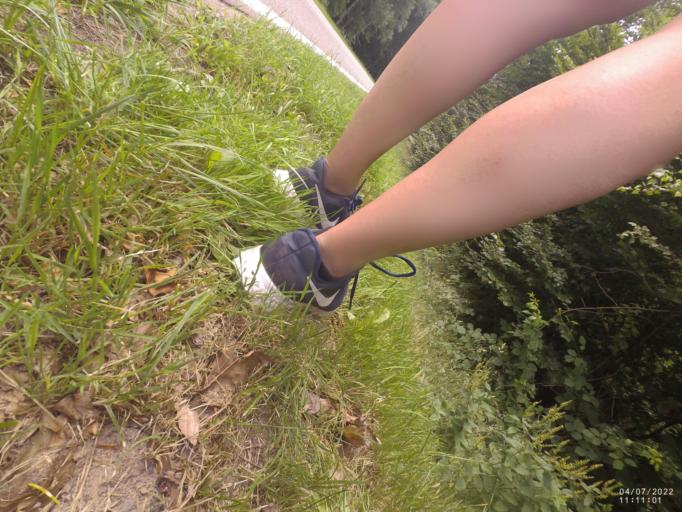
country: DE
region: Rheinland-Pfalz
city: Lindenberg
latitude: 49.4117
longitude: 8.1082
